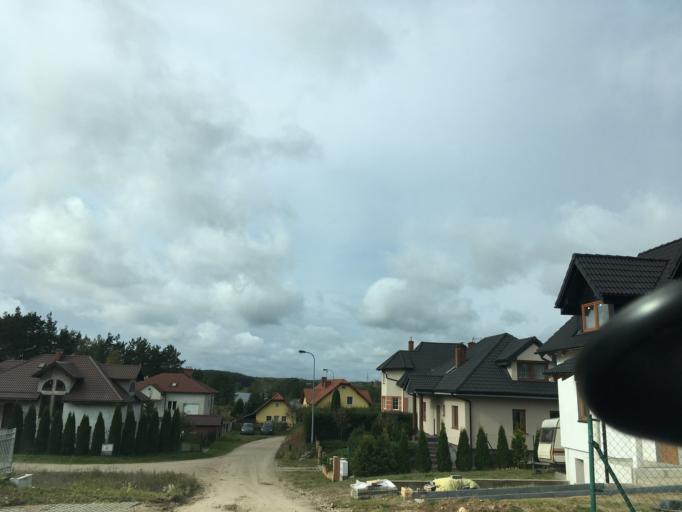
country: PL
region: Pomeranian Voivodeship
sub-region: Powiat koscierski
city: Koscierzyna
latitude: 54.1080
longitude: 18.0091
